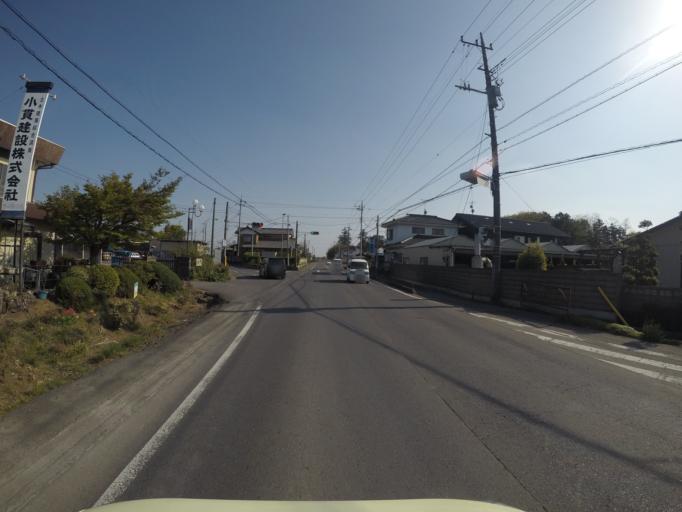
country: JP
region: Ibaraki
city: Yuki
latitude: 36.2452
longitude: 139.8722
